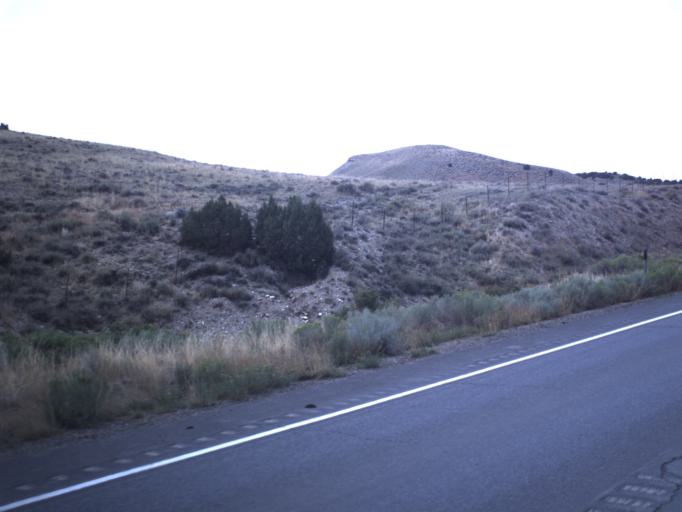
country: US
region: Utah
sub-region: Duchesne County
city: Duchesne
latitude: 40.1623
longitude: -110.2765
